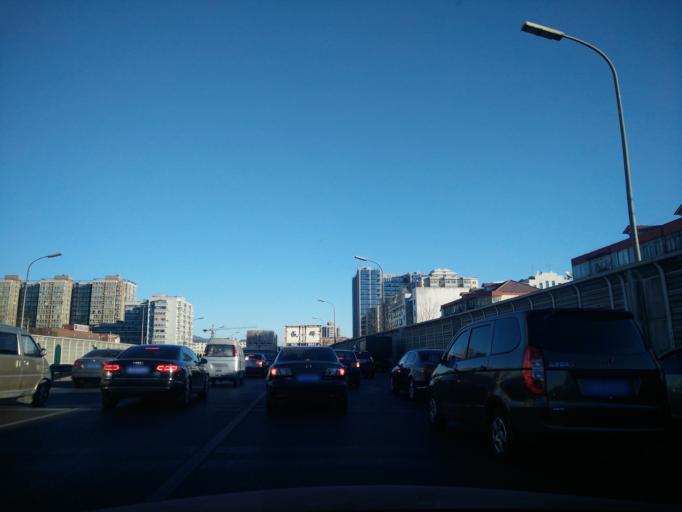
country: CN
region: Beijing
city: Lugu
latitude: 39.8975
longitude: 116.2052
